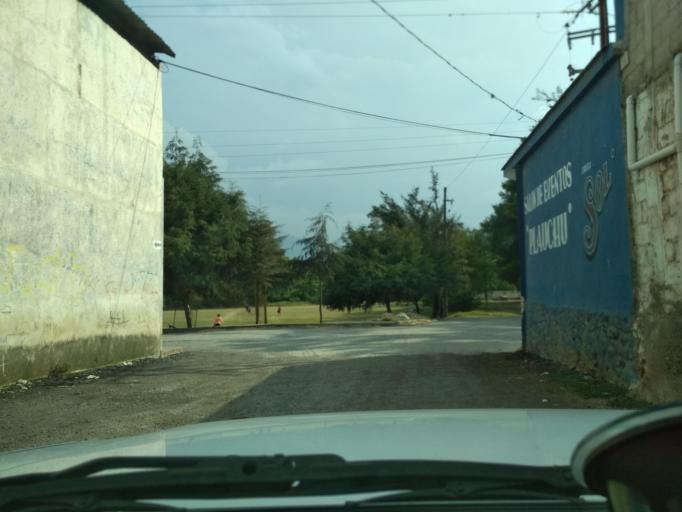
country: MX
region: Veracruz
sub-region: Nogales
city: Taza de Agua Ojo Zarco
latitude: 18.7939
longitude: -97.1975
